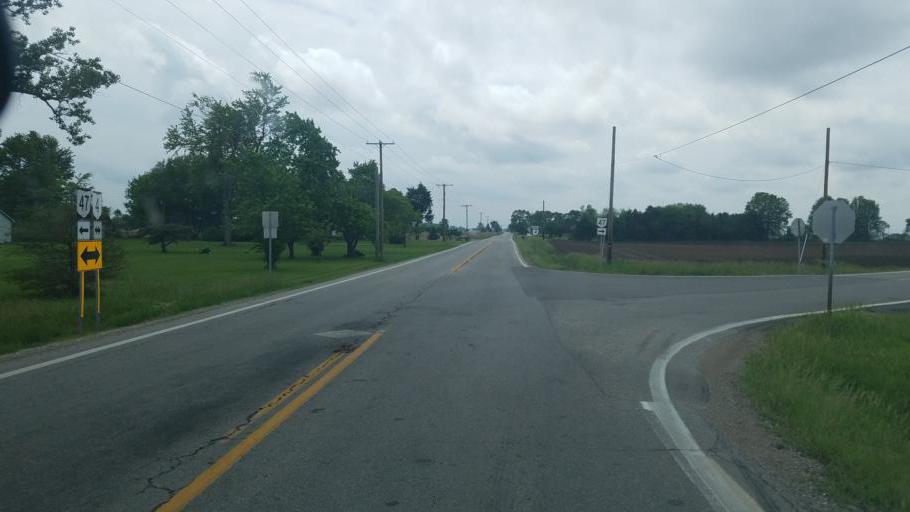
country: US
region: Ohio
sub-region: Marion County
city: Prospect
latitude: 40.4420
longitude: -83.2288
